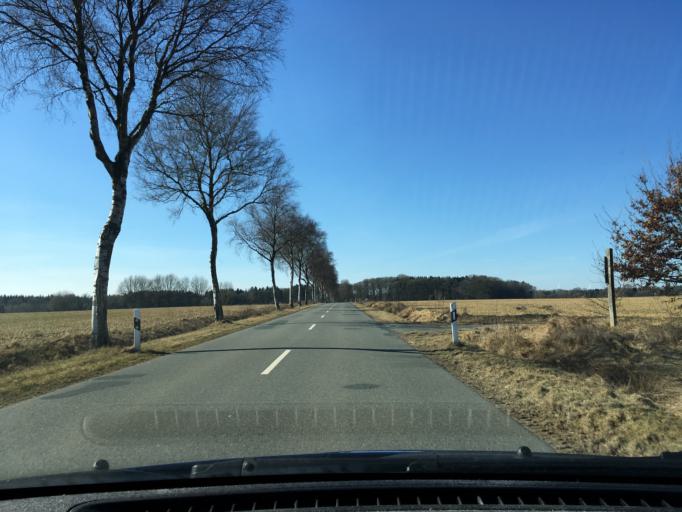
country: DE
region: Lower Saxony
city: Schneverdingen
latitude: 53.0822
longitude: 9.8334
